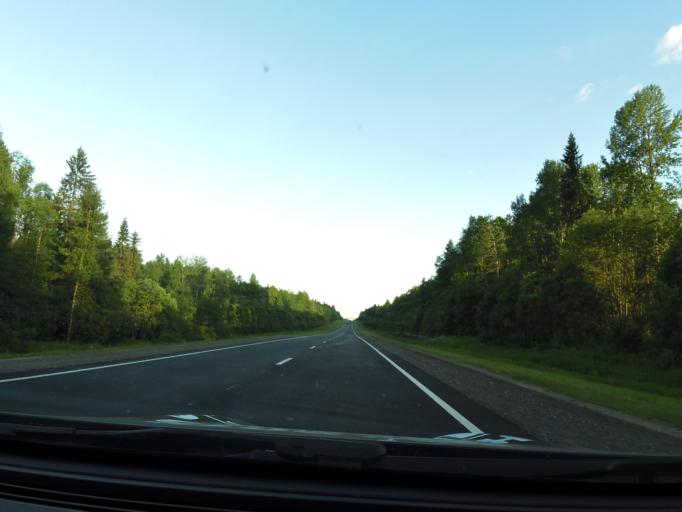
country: RU
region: Vologda
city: Gryazovets
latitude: 58.9052
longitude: 40.1817
